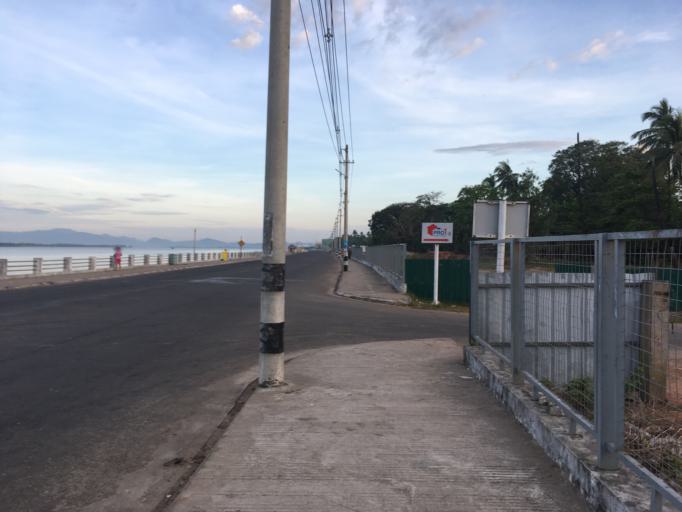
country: MM
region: Mon
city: Mawlamyine
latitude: 16.4584
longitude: 97.6235
